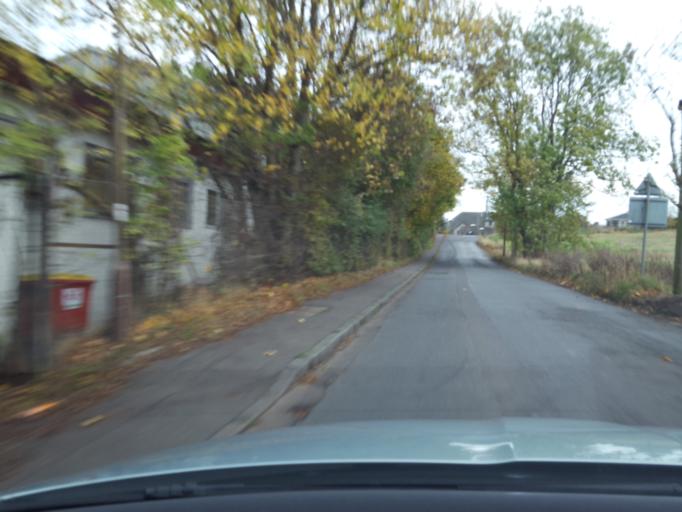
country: GB
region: Scotland
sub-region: Edinburgh
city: Ratho
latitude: 55.9263
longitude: -3.3810
